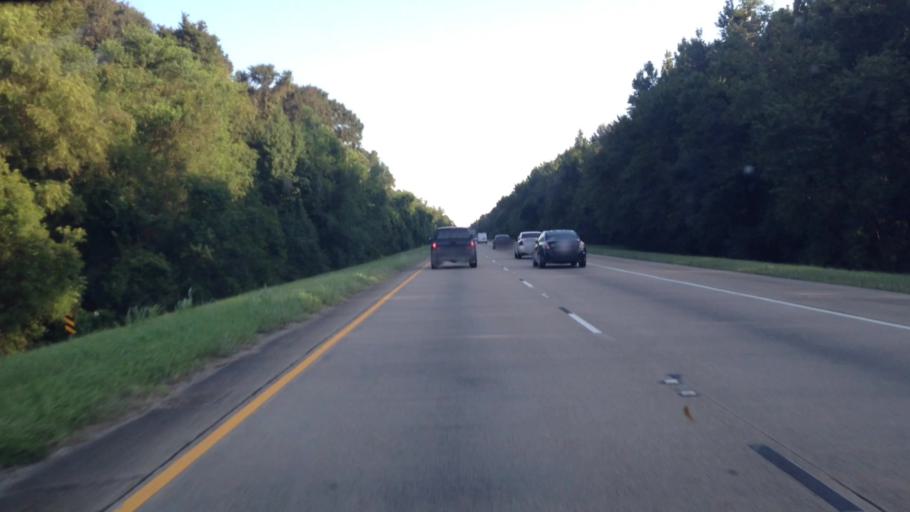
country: US
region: Louisiana
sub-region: Ascension Parish
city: Prairieville
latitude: 30.2871
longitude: -90.9898
